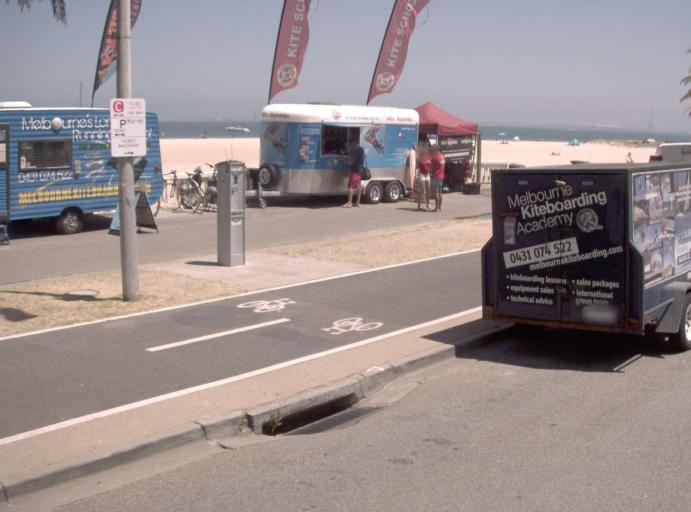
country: AU
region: Victoria
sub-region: Port Phillip
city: St Kilda West
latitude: -37.8577
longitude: 144.9679
